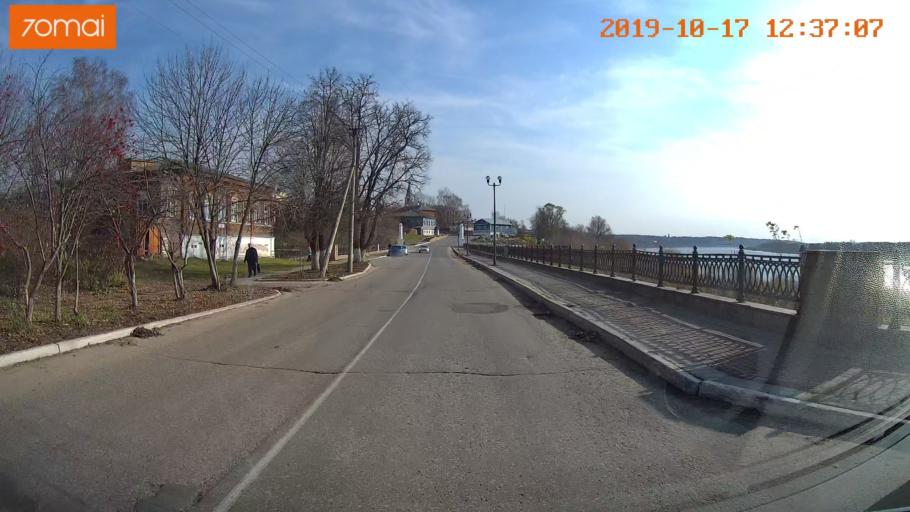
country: RU
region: Rjazan
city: Kasimov
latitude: 54.9375
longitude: 41.3833
